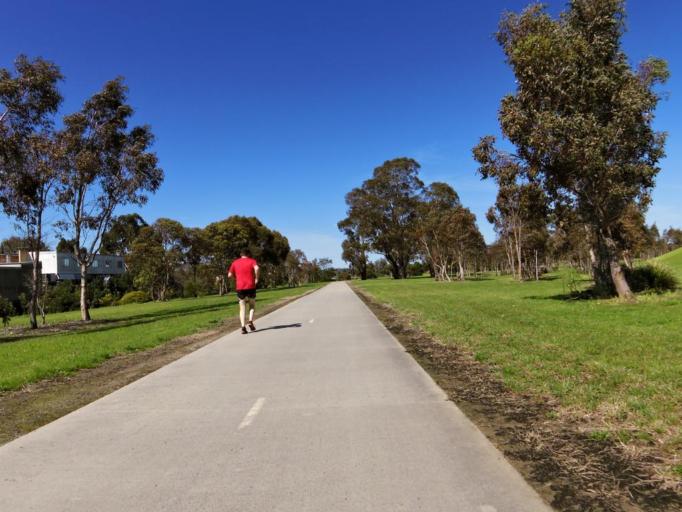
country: AU
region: Victoria
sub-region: Greater Dandenong
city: Dandenong
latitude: -37.9971
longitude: 145.1933
